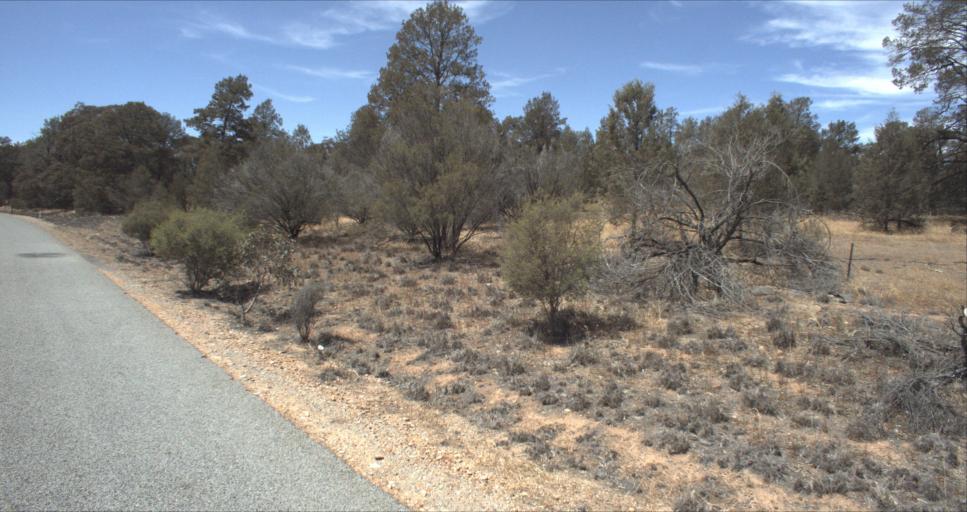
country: AU
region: New South Wales
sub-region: Leeton
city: Leeton
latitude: -34.6715
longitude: 146.4410
